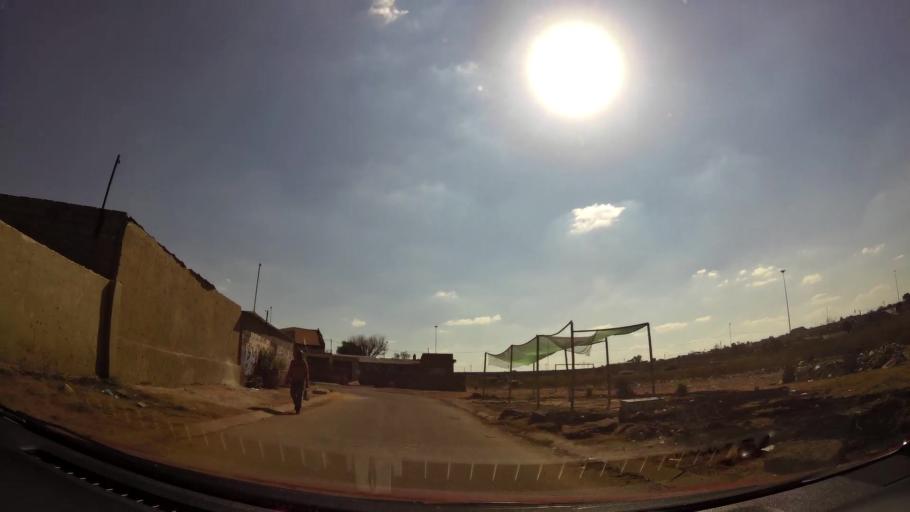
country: ZA
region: Gauteng
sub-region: City of Johannesburg Metropolitan Municipality
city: Soweto
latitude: -26.2298
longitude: 27.8847
